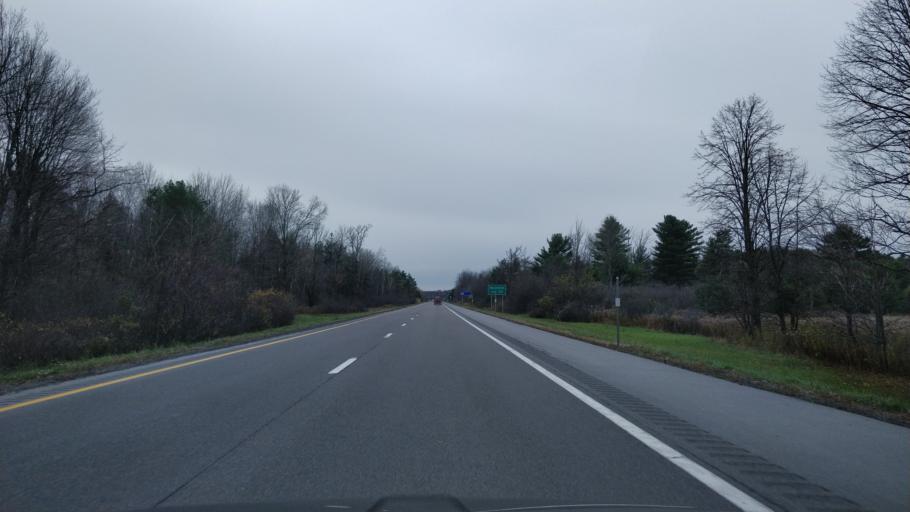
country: US
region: New York
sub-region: Oswego County
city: Pulaski
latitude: 43.6650
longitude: -76.0724
